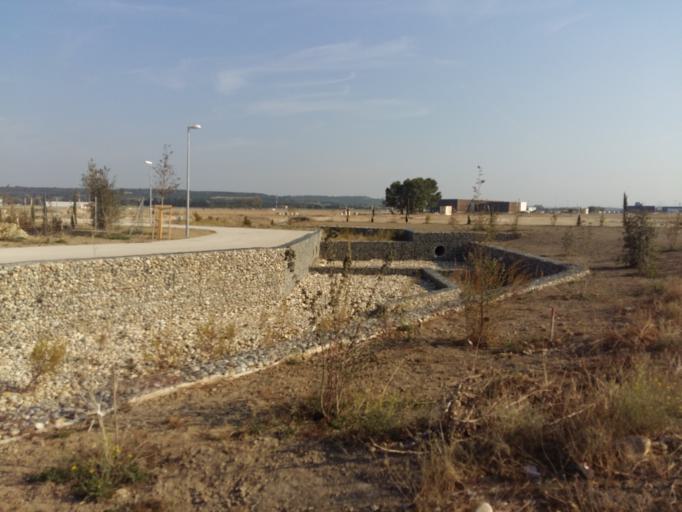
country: FR
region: Provence-Alpes-Cote d'Azur
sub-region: Departement du Vaucluse
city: Morieres-les-Avignon
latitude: 43.9130
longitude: 4.8944
